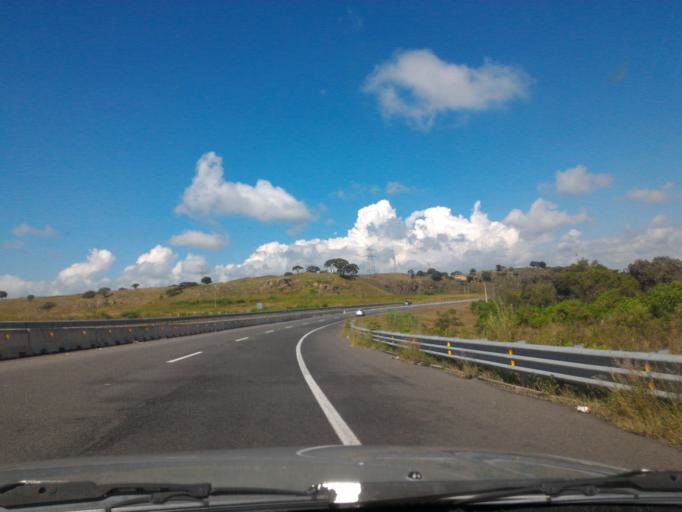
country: MX
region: Jalisco
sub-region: Tala
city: Los Ruisenores
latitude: 20.7319
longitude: -103.6203
